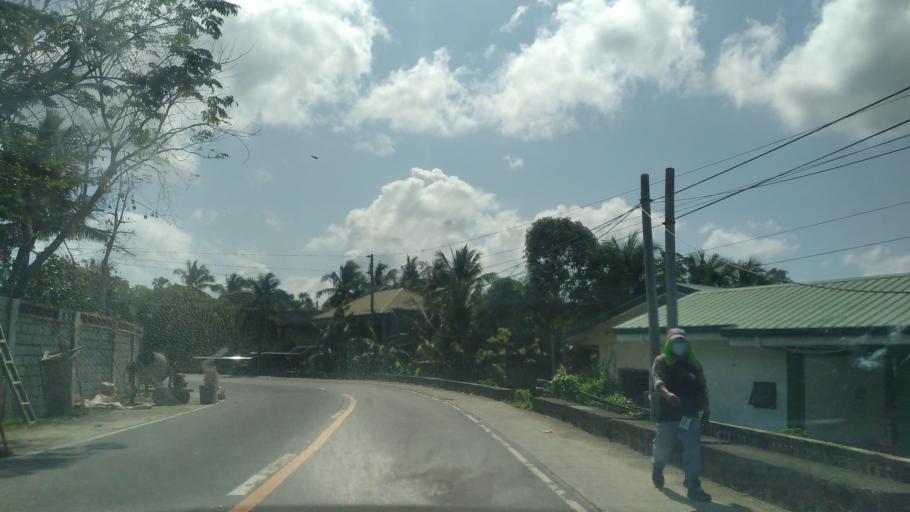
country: PH
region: Calabarzon
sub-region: Province of Quezon
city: Unisan
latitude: 13.8337
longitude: 121.9805
